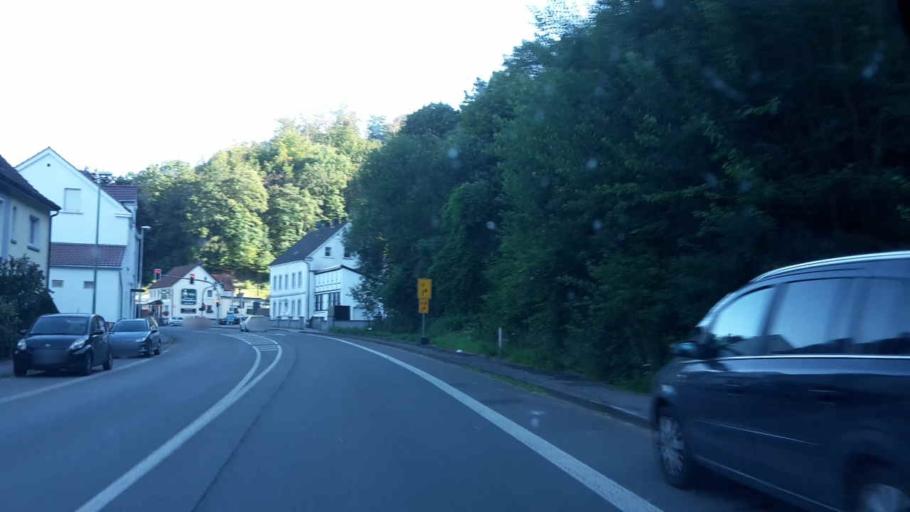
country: DE
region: North Rhine-Westphalia
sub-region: Regierungsbezirk Arnsberg
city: Nachrodt-Wiblingwerde
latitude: 51.3590
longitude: 7.5524
